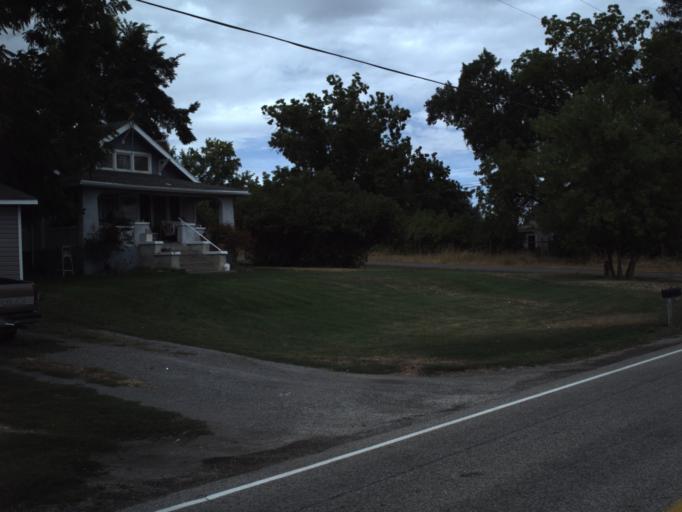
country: US
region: Utah
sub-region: Cache County
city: Mendon
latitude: 41.7054
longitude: -111.9794
